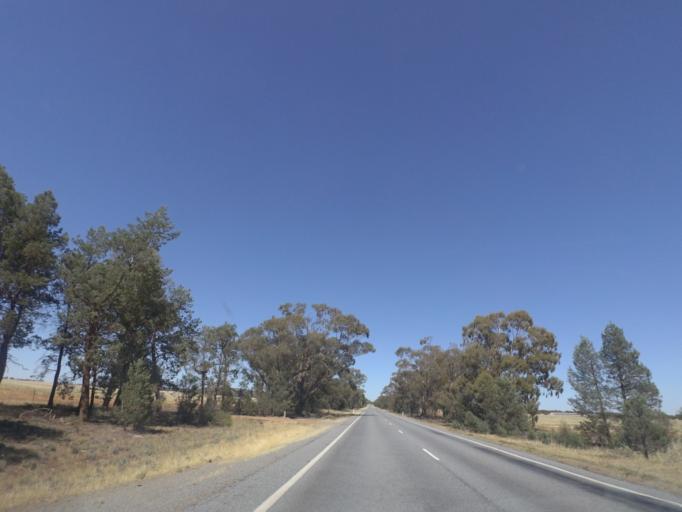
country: AU
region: New South Wales
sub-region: Narrandera
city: Narrandera
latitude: -34.4154
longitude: 146.8612
